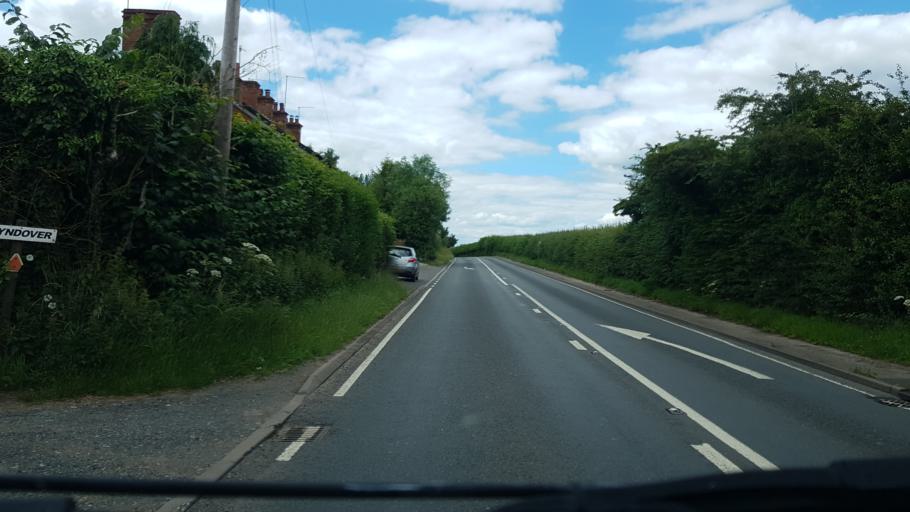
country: GB
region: England
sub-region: Worcestershire
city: Stourport-on-Severn
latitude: 52.3234
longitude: -2.2487
